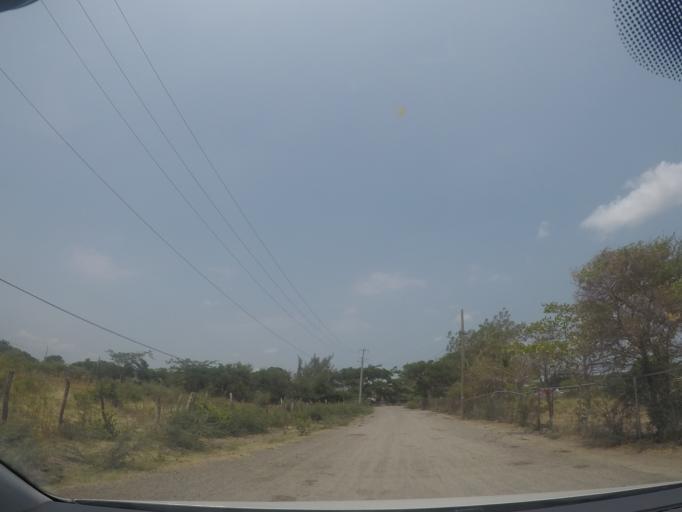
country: MX
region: Oaxaca
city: Asuncion Ixtaltepec
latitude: 16.5053
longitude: -95.0669
